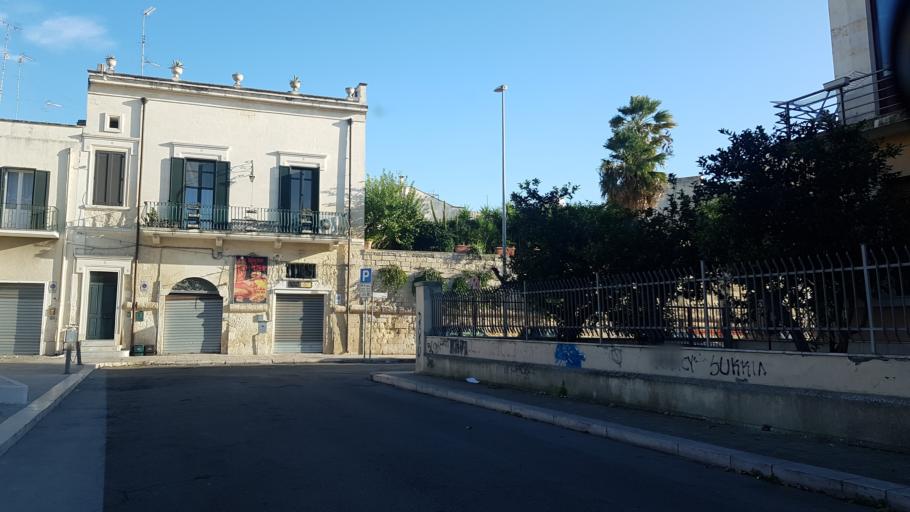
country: IT
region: Apulia
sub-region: Provincia di Lecce
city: Lecce
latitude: 40.3524
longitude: 18.1649
